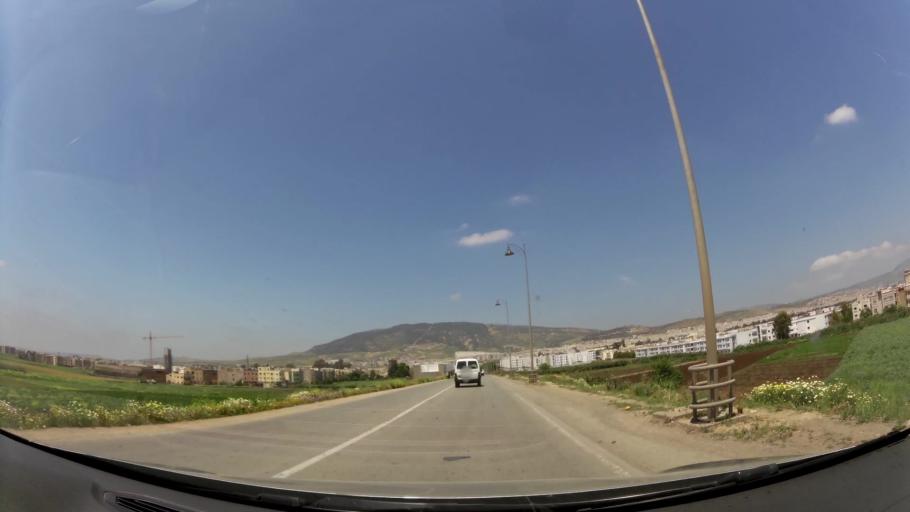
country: MA
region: Fes-Boulemane
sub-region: Fes
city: Fes
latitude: 34.0335
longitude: -5.0310
